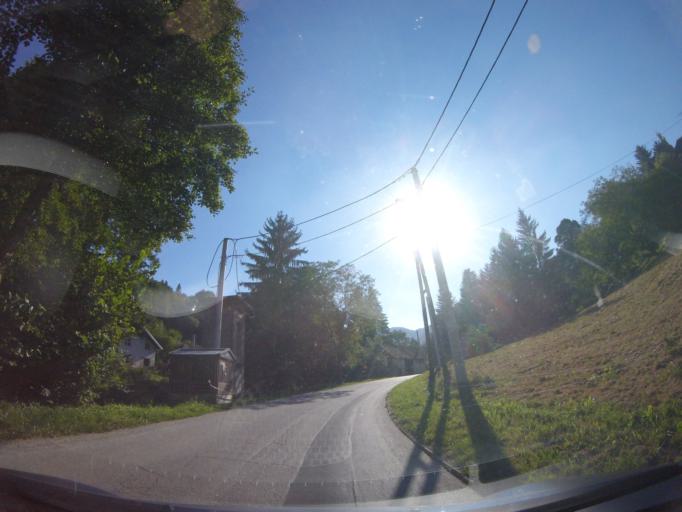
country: HR
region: Zagrebacka
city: Rude
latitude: 45.7645
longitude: 15.6705
